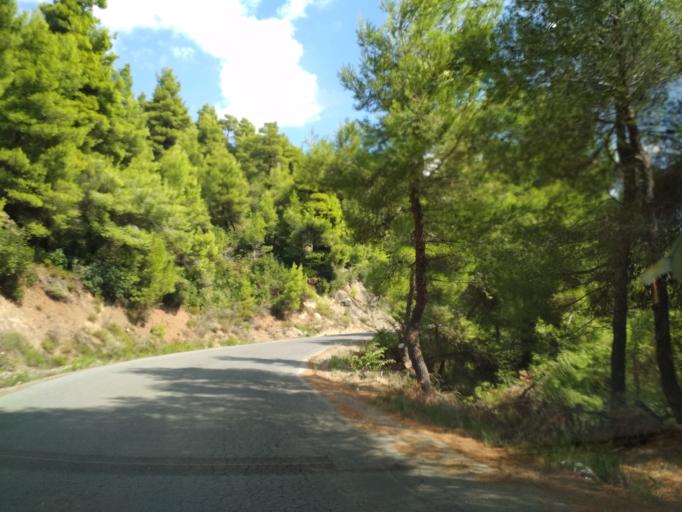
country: GR
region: Central Greece
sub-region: Nomos Evvoias
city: Roviai
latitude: 38.8338
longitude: 23.2849
